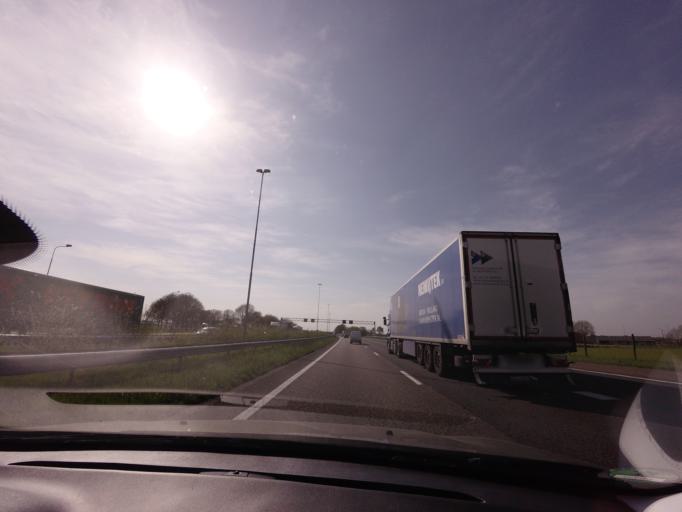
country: NL
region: North Brabant
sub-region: Gemeente Dongen
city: Dongen
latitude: 51.5592
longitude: 4.8828
